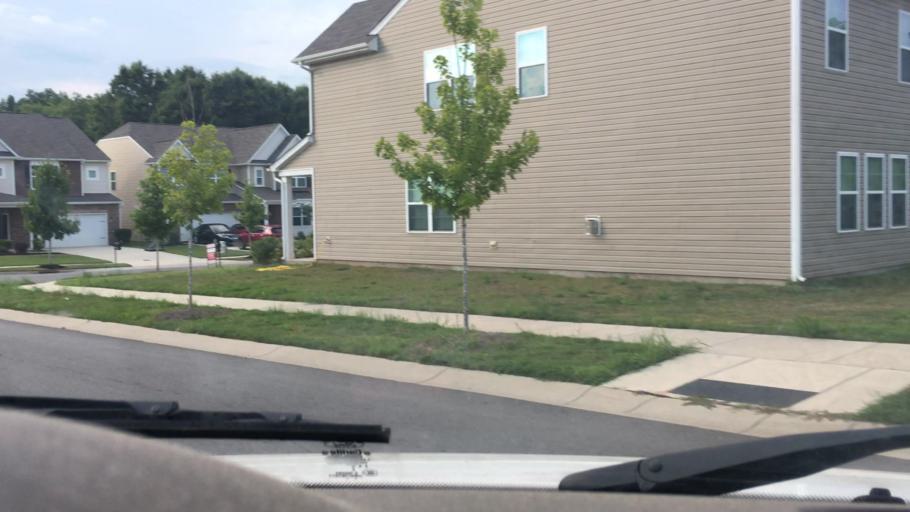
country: US
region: North Carolina
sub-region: Mecklenburg County
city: Huntersville
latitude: 35.4223
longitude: -80.7479
